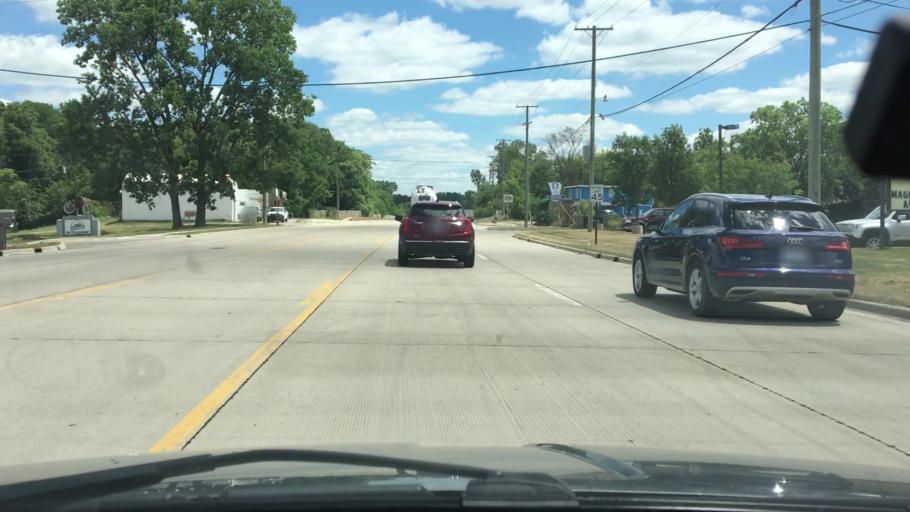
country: US
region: Michigan
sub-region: Livingston County
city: Brighton
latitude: 42.5177
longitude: -83.7440
